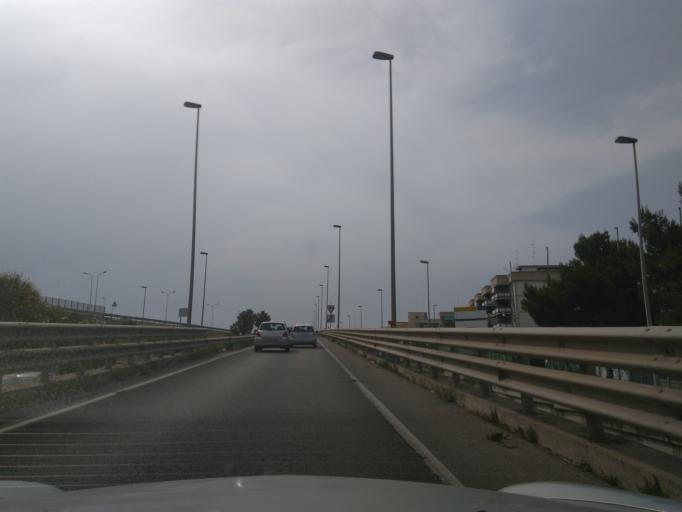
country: IT
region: Apulia
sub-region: Provincia di Bari
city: San Paolo
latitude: 41.1350
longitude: 16.8153
